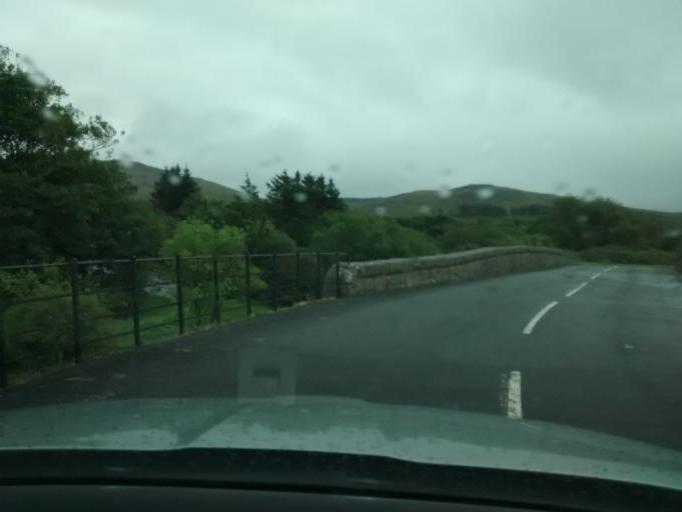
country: GB
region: Scotland
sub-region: North Ayrshire
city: Isle of Arran
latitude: 55.5802
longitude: -5.3601
